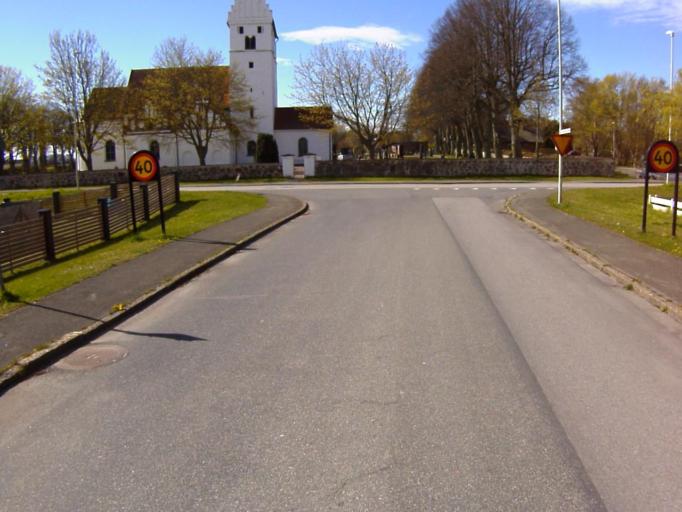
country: SE
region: Skane
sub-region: Kristianstads Kommun
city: Norra Asum
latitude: 55.9904
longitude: 14.1514
